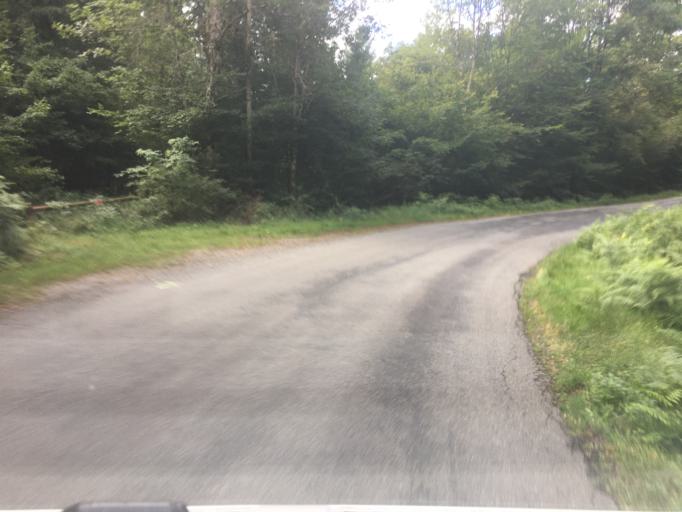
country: FR
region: Limousin
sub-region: Departement de la Correze
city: Neuvic
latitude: 45.4259
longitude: 2.3559
